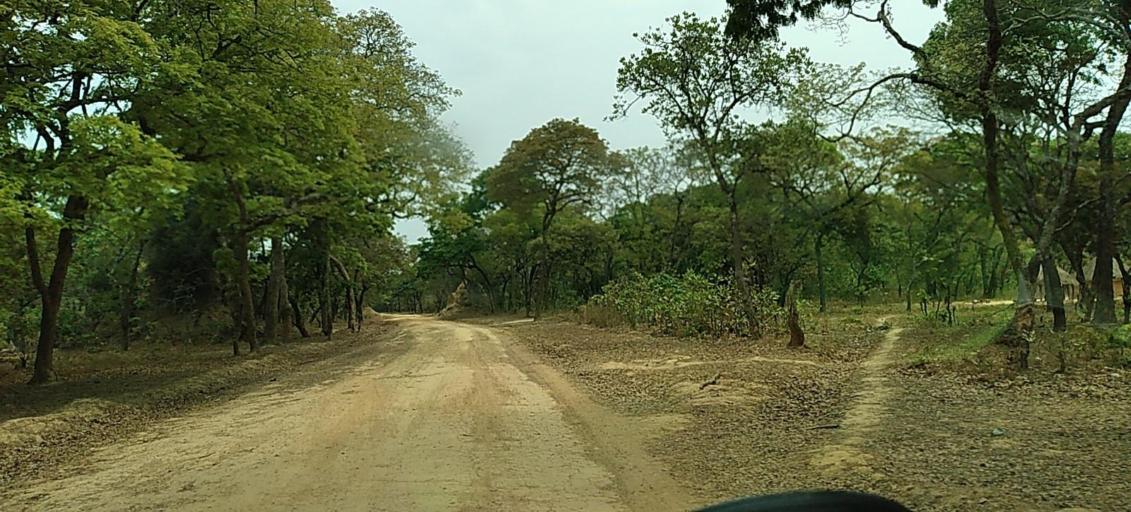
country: ZM
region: North-Western
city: Solwezi
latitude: -12.9322
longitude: 26.5599
